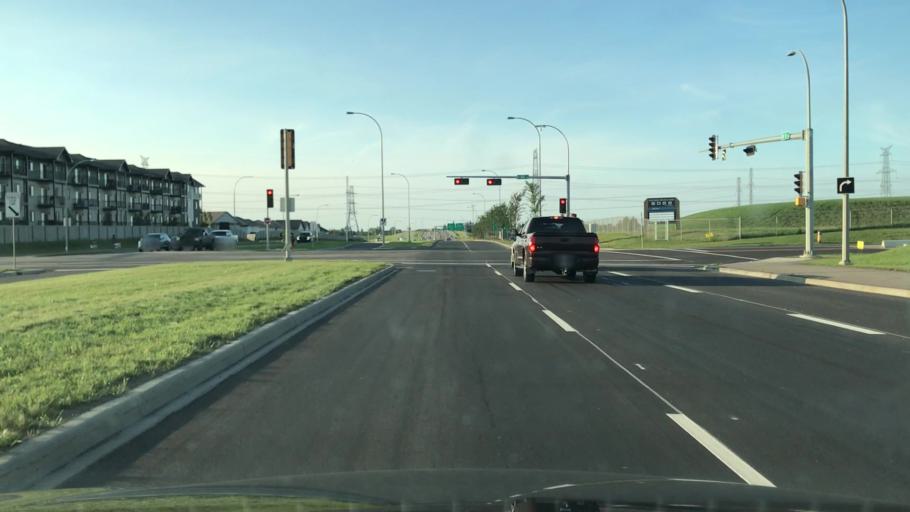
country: CA
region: Alberta
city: Beaumont
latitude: 53.4280
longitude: -113.4178
